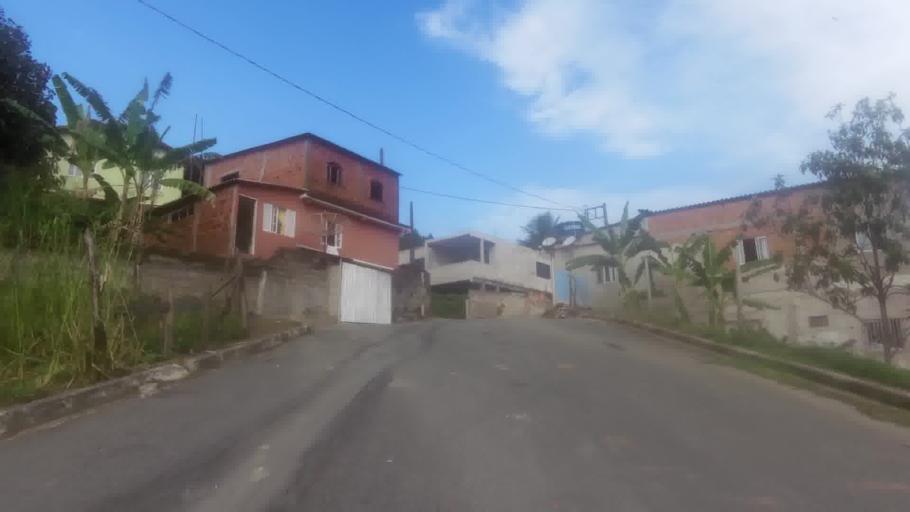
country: BR
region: Espirito Santo
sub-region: Guarapari
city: Guarapari
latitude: -20.7679
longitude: -40.5763
